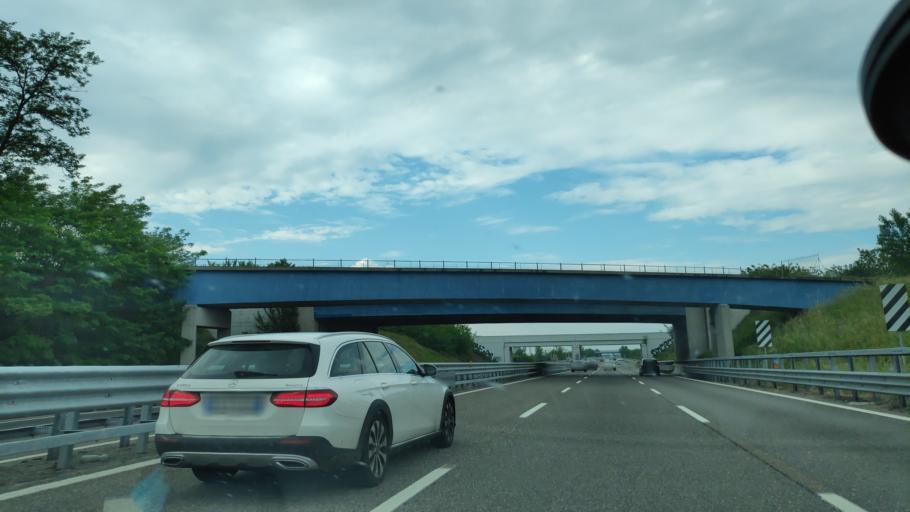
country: IT
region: Lombardy
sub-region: Provincia di Pavia
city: Pieve Albignola
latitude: 45.1172
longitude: 8.9766
